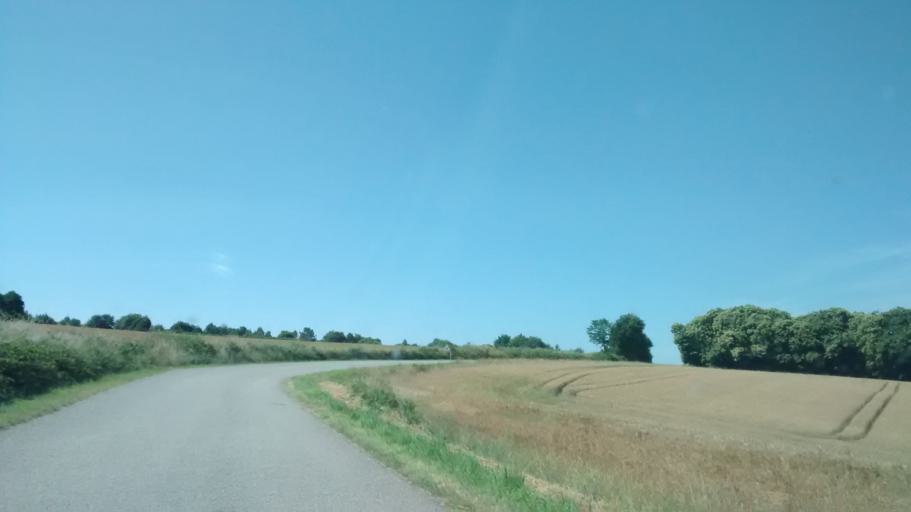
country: FR
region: Brittany
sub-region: Departement du Morbihan
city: Campeneac
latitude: 47.9959
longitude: -2.3010
